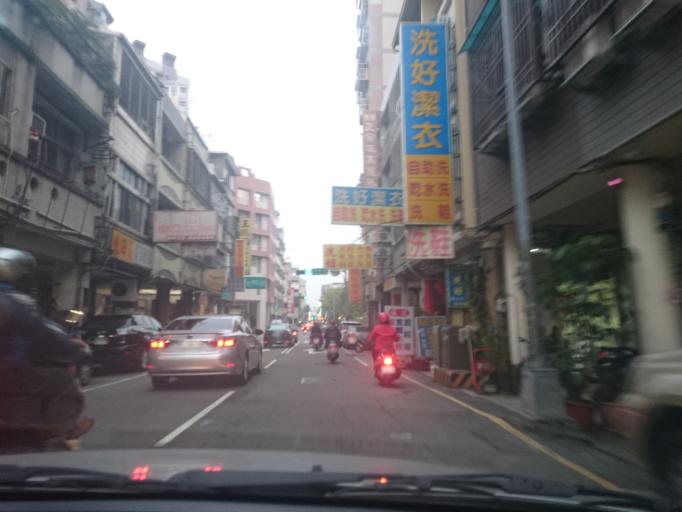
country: TW
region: Taiwan
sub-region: Taichung City
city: Taichung
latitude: 24.1452
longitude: 120.6779
